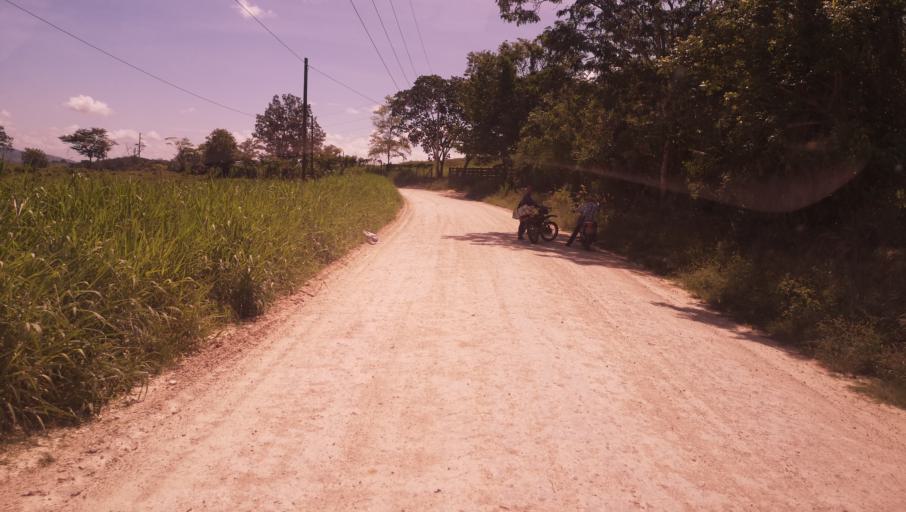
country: GT
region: Peten
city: Melchor de Mencos
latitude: 16.9845
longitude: -89.2581
